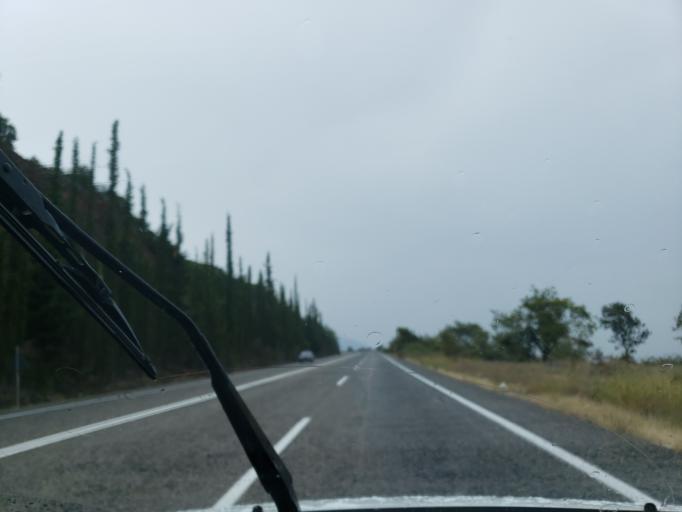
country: GR
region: Central Greece
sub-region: Nomos Fthiotidos
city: Anthili
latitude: 38.7933
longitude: 22.4795
